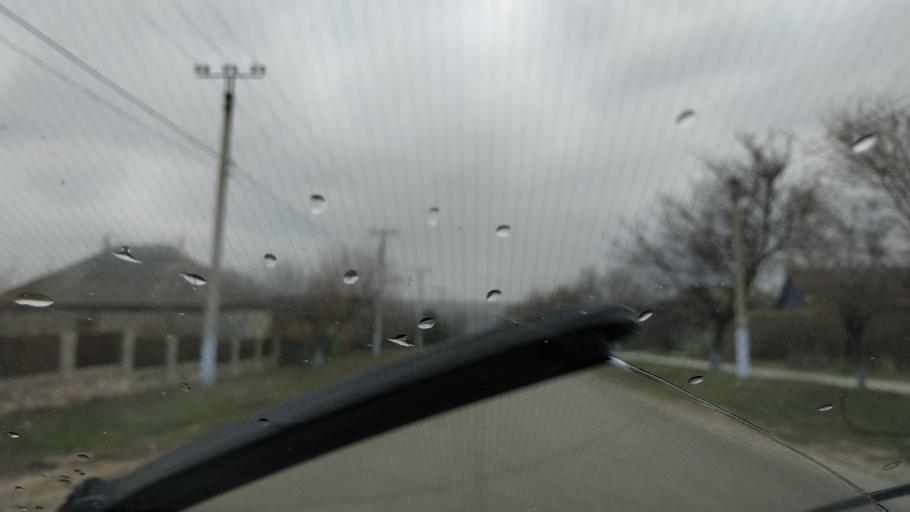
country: MD
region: Gagauzia
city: Comrat
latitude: 46.2430
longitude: 28.7663
